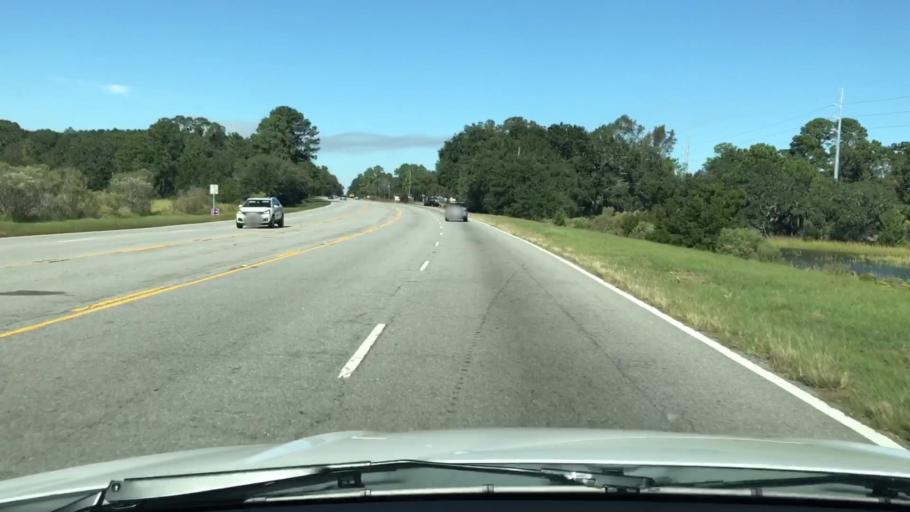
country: US
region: South Carolina
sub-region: Beaufort County
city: Laurel Bay
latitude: 32.5454
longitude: -80.7442
